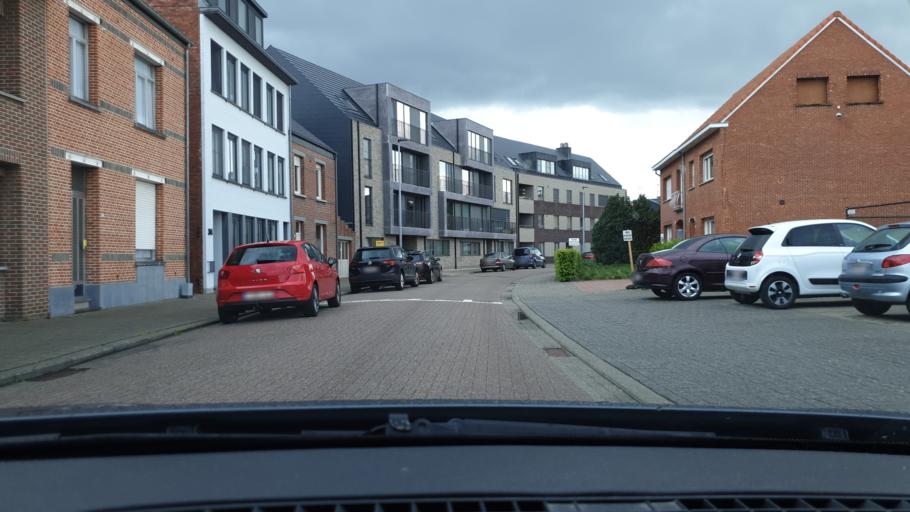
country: BE
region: Flanders
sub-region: Provincie Antwerpen
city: Geel
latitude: 51.1643
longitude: 5.0046
